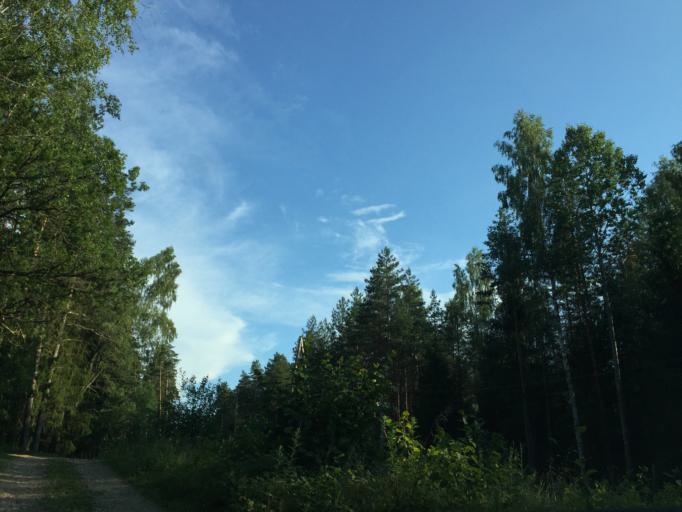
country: LV
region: Krimulda
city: Ragana
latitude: 57.1424
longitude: 24.7648
